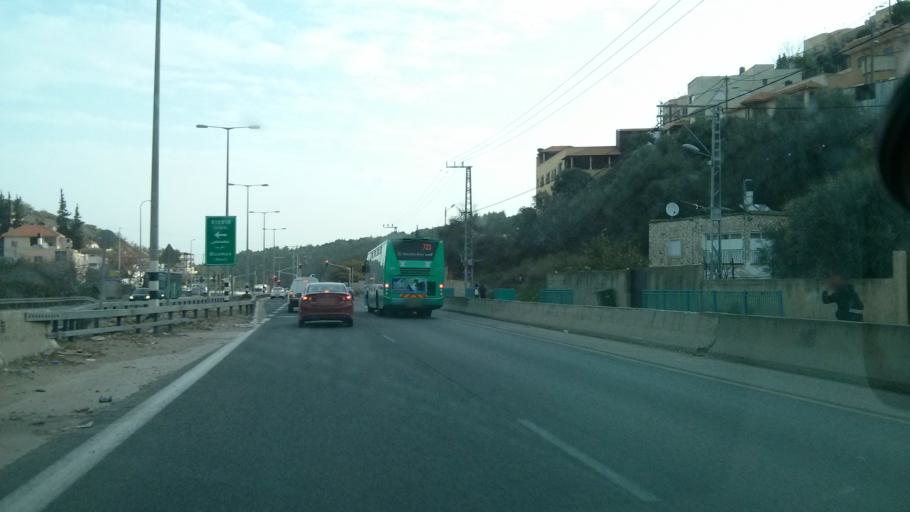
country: IL
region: Haifa
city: Umm el Fahm
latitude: 32.5407
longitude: 35.1553
